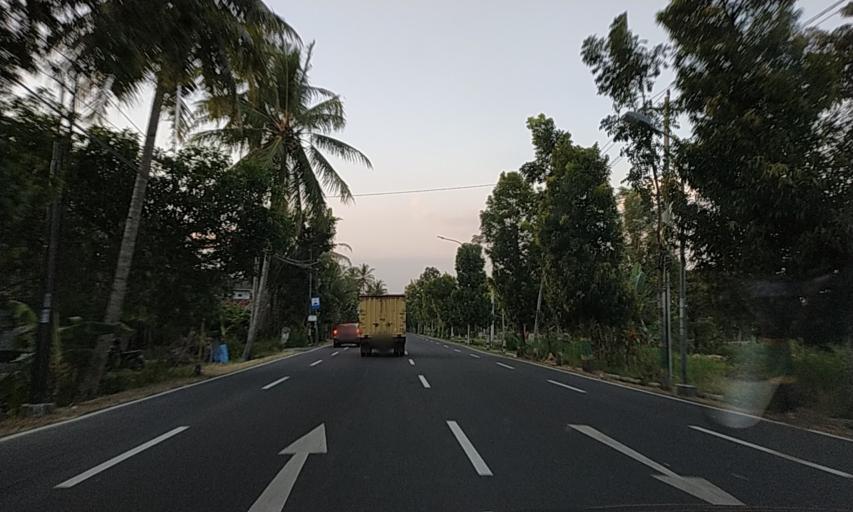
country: ID
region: Daerah Istimewa Yogyakarta
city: Srandakan
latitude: -7.8821
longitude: 110.1317
